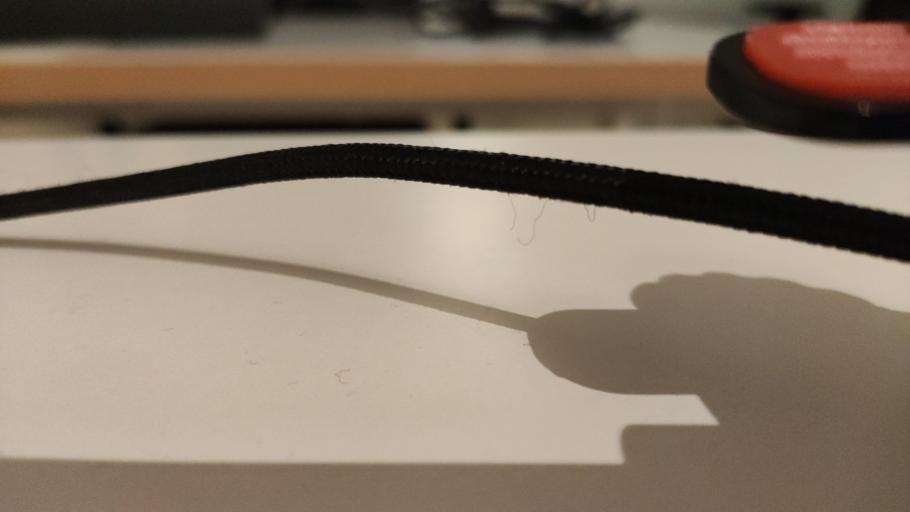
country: RU
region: Moskovskaya
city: Novoye
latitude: 55.6567
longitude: 38.9373
